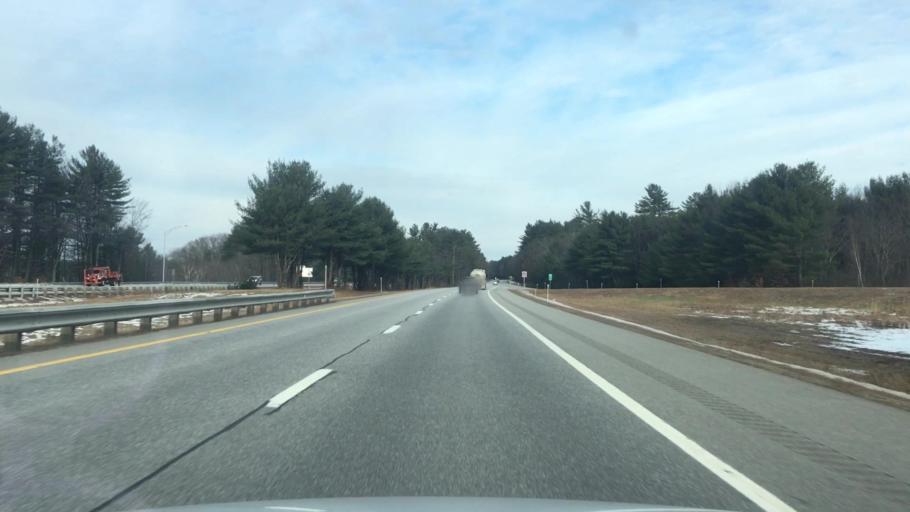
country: US
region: New Hampshire
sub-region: Merrimack County
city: Contoocook
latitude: 43.2040
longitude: -71.7086
